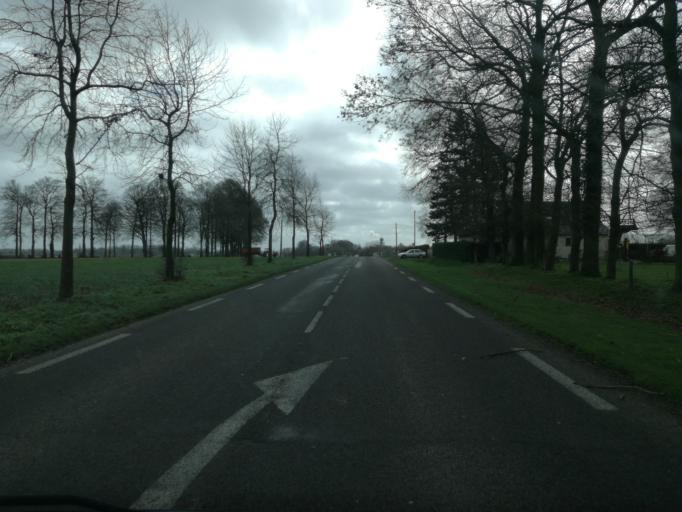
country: FR
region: Haute-Normandie
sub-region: Departement de la Seine-Maritime
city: Valliquerville
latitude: 49.6189
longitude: 0.6562
